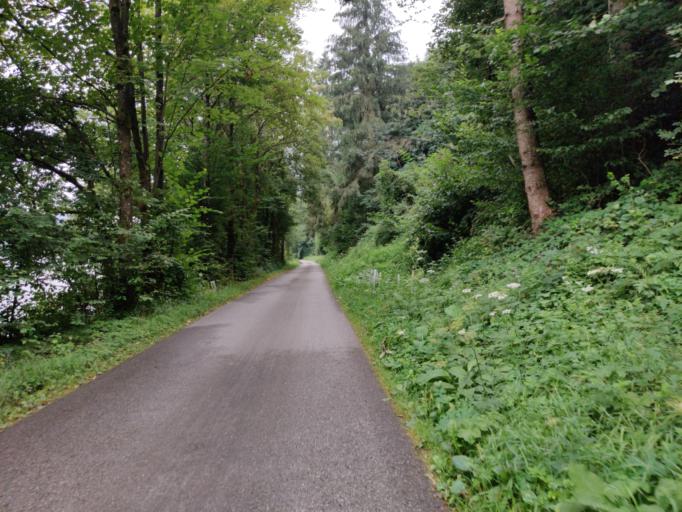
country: AT
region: Lower Austria
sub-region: Politischer Bezirk Melk
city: Nochling
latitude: 48.2157
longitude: 14.9505
